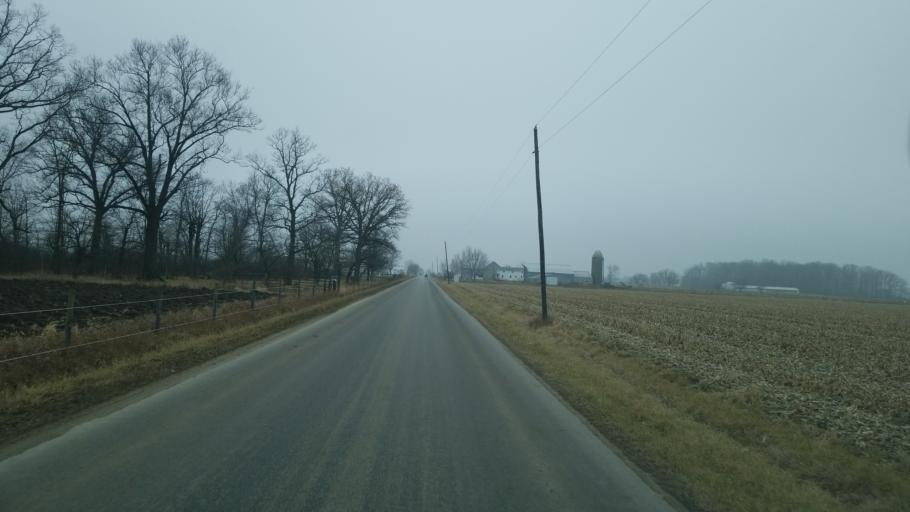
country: US
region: Indiana
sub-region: Adams County
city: Berne
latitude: 40.7303
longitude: -84.9175
